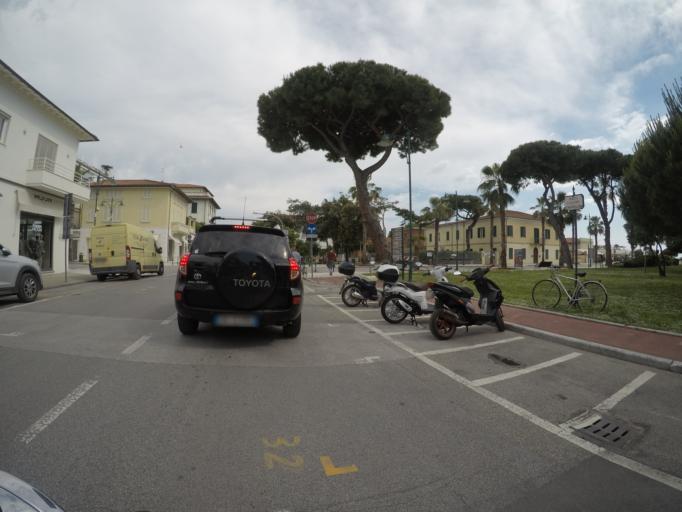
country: IT
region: Tuscany
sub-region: Provincia di Lucca
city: Forte dei Marmi
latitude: 43.9588
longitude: 10.1681
